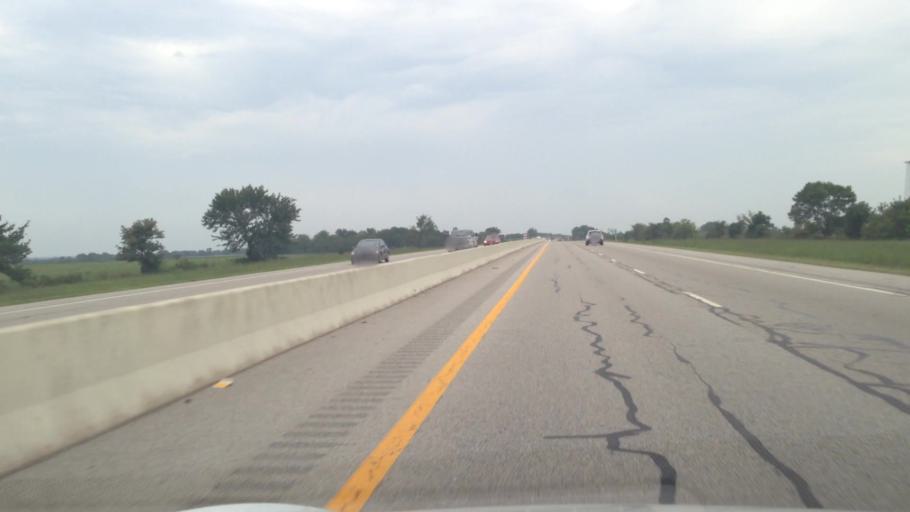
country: US
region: Oklahoma
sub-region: Ottawa County
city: Fairland
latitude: 36.7541
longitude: -94.9022
